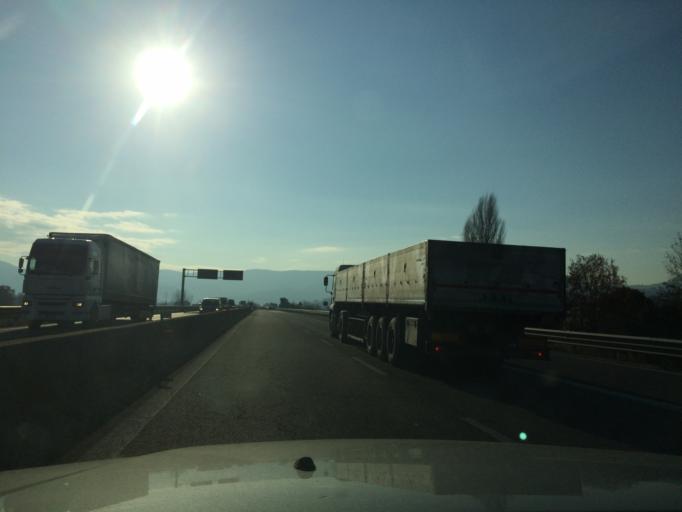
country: IT
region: Umbria
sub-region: Provincia di Terni
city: Narni Scalo
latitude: 42.5560
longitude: 12.5353
